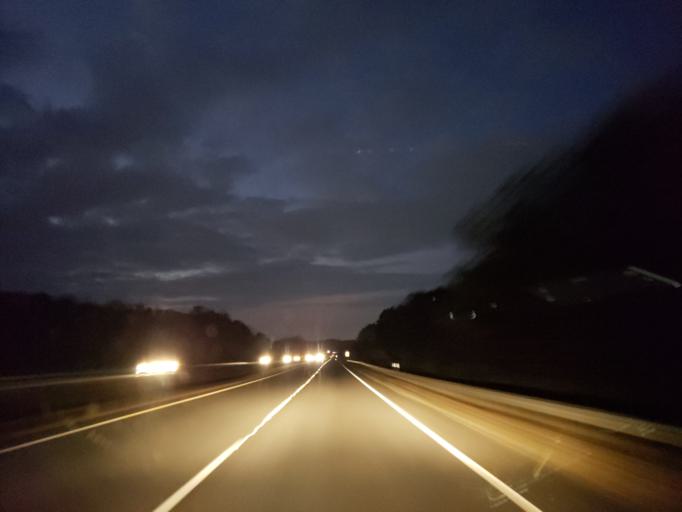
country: US
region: Georgia
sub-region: Polk County
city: Rockmart
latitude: 33.9825
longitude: -85.0139
